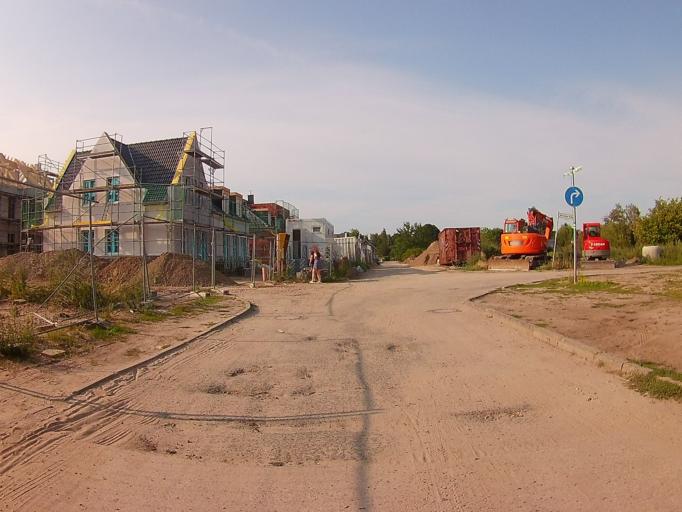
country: DE
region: Berlin
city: Kaulsdorf
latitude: 52.5026
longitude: 13.5772
